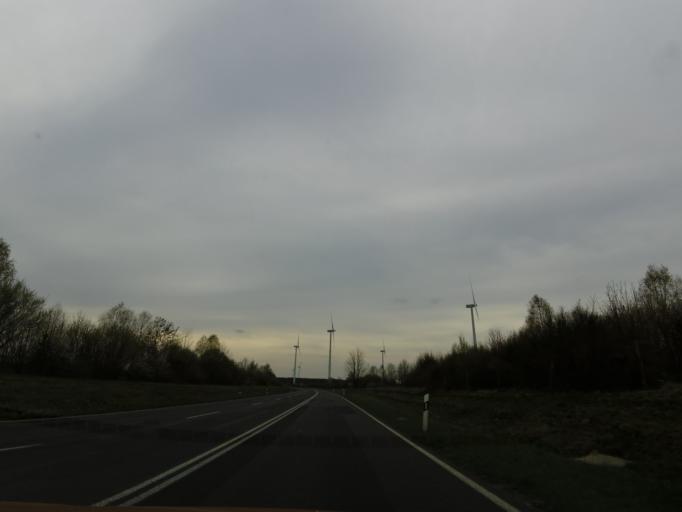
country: DE
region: Brandenburg
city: Beeskow
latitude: 52.2002
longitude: 14.2526
